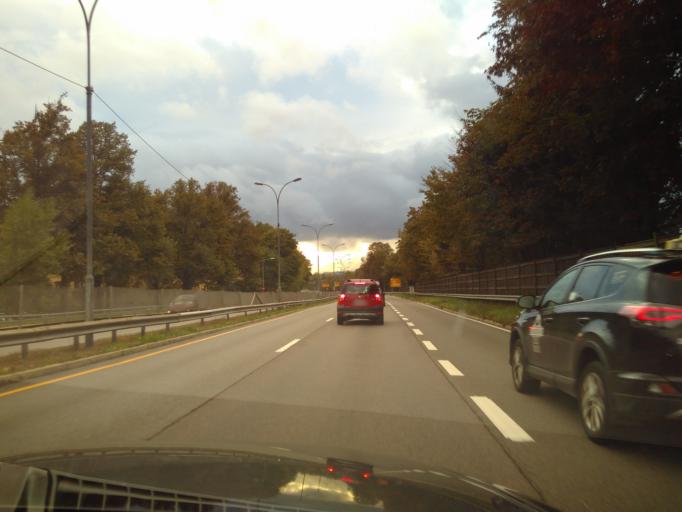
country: NO
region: Oslo
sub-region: Oslo
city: Oslo
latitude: 59.9402
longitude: 10.7939
